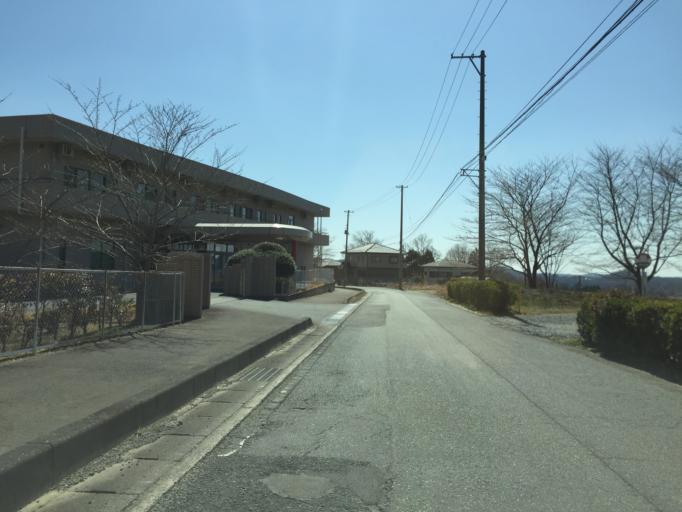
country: JP
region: Fukushima
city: Iwaki
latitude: 37.0520
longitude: 140.8421
